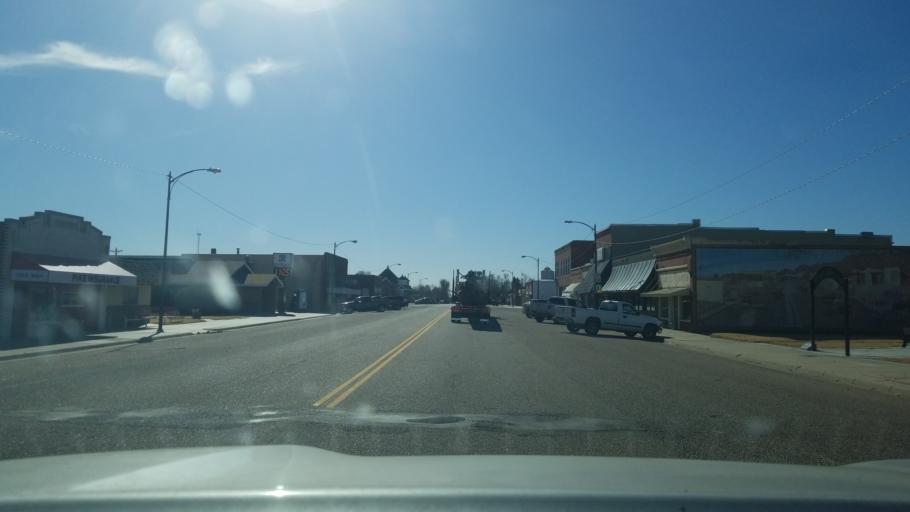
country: US
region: Kansas
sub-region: Kiowa County
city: Greensburg
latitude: 37.5506
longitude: -99.6341
